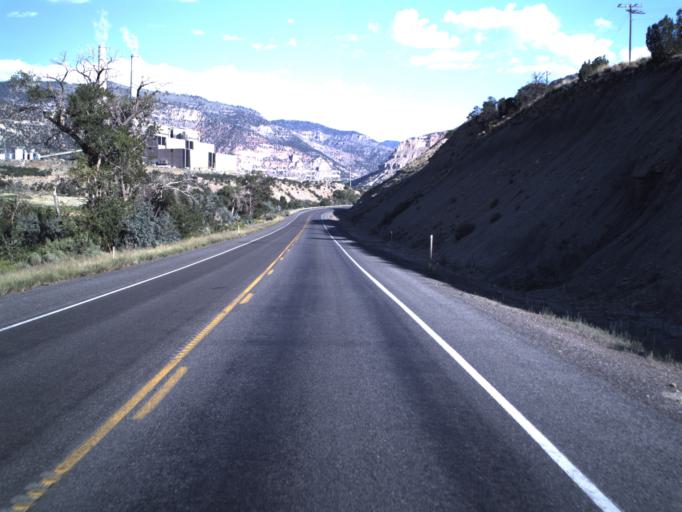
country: US
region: Utah
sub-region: Emery County
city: Huntington
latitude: 39.3746
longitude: -111.0646
